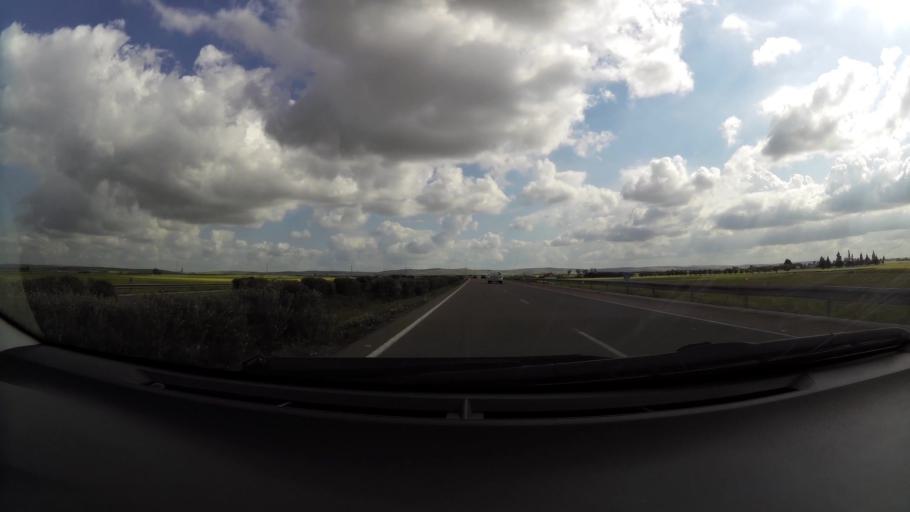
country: MA
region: Chaouia-Ouardigha
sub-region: Settat Province
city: Settat
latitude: 33.1288
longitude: -7.5790
